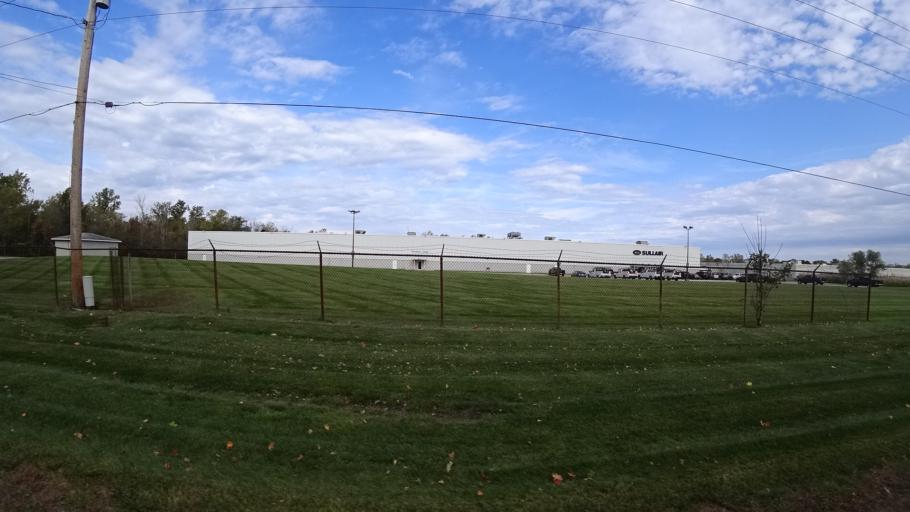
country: US
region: Indiana
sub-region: LaPorte County
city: Michigan City
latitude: 41.6659
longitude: -86.9079
